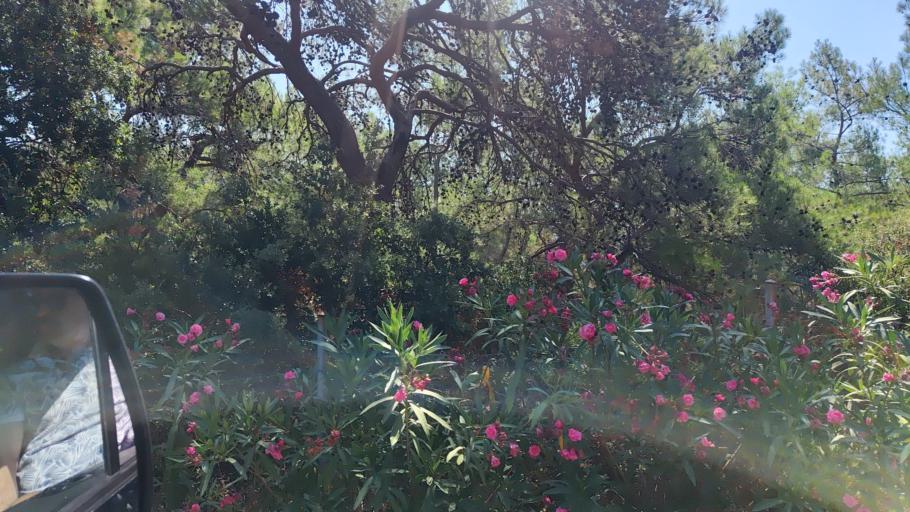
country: TR
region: Mugla
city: Sarigerme
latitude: 36.7060
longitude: 28.6955
